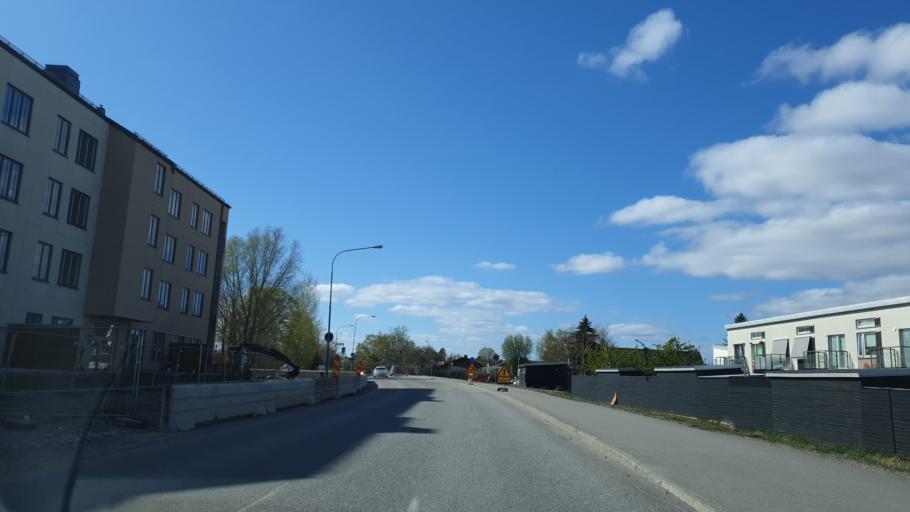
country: SE
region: Uppsala
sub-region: Uppsala Kommun
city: Gamla Uppsala
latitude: 59.8915
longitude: 17.6505
